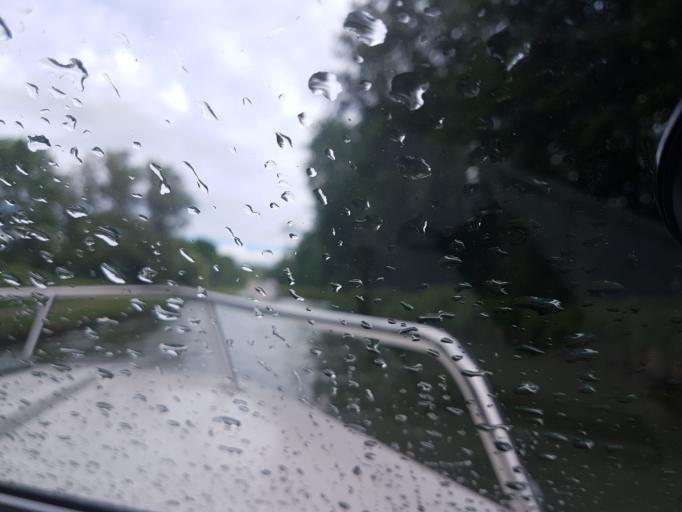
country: FR
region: Bourgogne
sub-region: Departement de la Nievre
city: Clamecy
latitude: 47.5460
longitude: 3.6324
